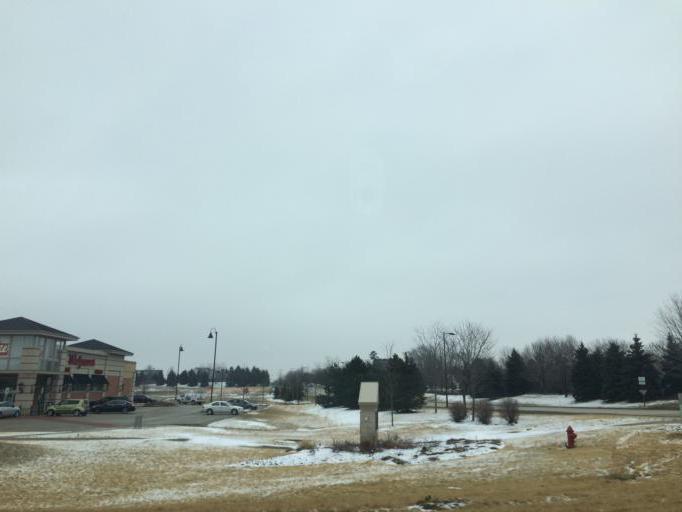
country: US
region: Illinois
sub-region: McHenry County
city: Huntley
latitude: 42.1832
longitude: -88.4224
